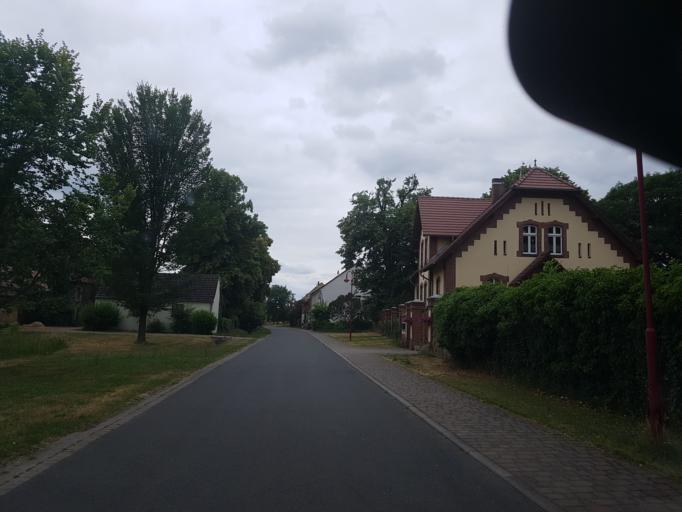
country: DE
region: Saxony-Anhalt
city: Seyda
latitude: 51.9532
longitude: 12.9149
